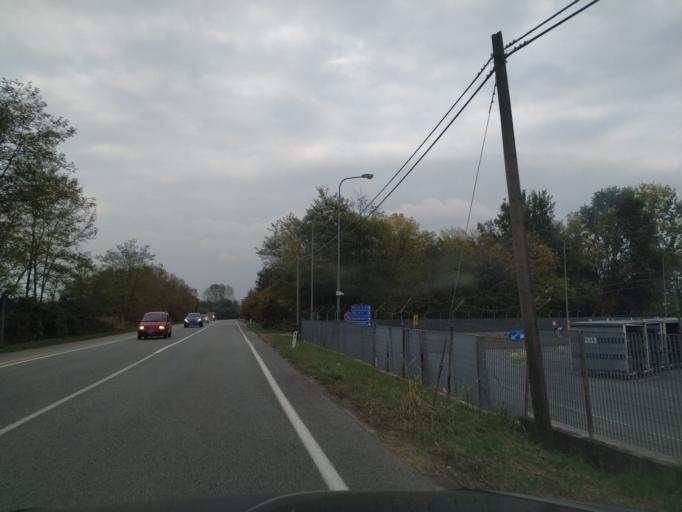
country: IT
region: Piedmont
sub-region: Provincia di Torino
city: San Benigno Canavese
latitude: 45.2142
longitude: 7.8062
